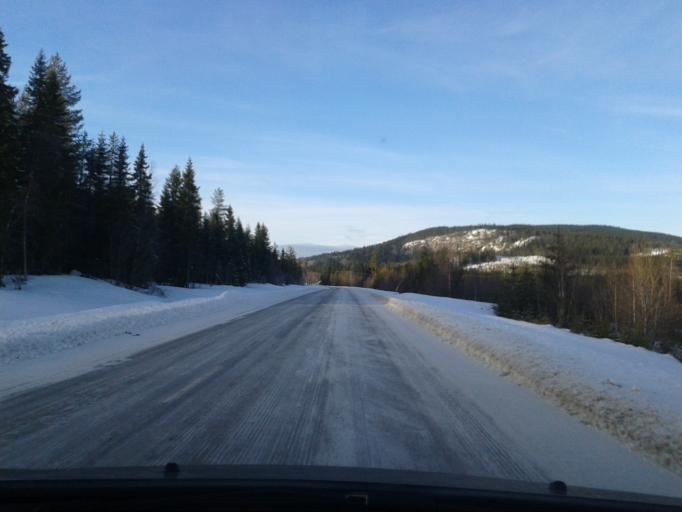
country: SE
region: Vaesterbotten
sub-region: Asele Kommun
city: Asele
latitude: 63.7784
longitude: 17.6679
